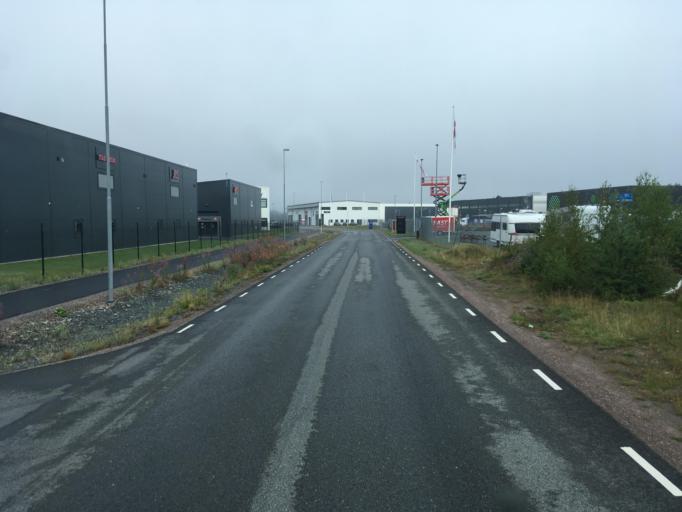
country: SE
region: Joenkoeping
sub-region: Jonkopings Kommun
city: Jonkoping
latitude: 57.7671
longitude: 14.0863
